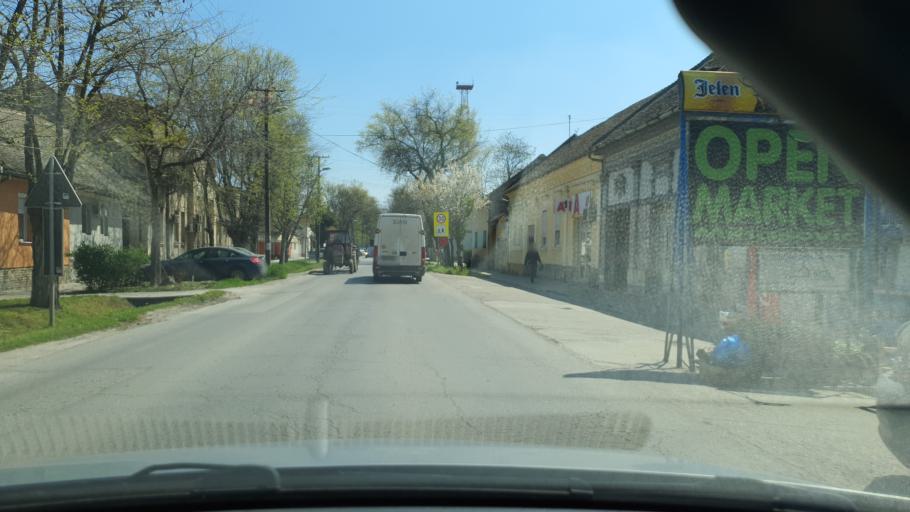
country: RS
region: Autonomna Pokrajina Vojvodina
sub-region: Zapadnobacki Okrug
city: Odzaci
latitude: 45.5086
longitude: 19.2562
